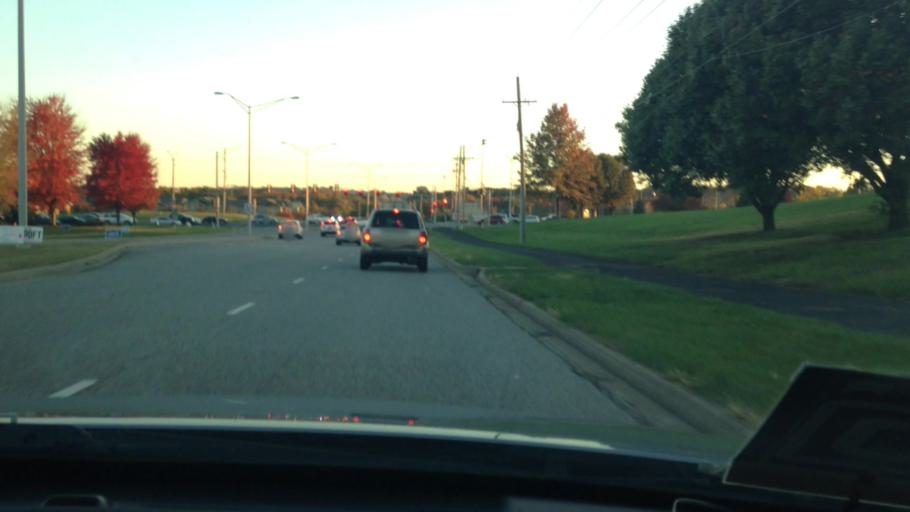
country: US
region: Kansas
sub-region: Johnson County
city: Lenexa
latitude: 38.8853
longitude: -94.7006
